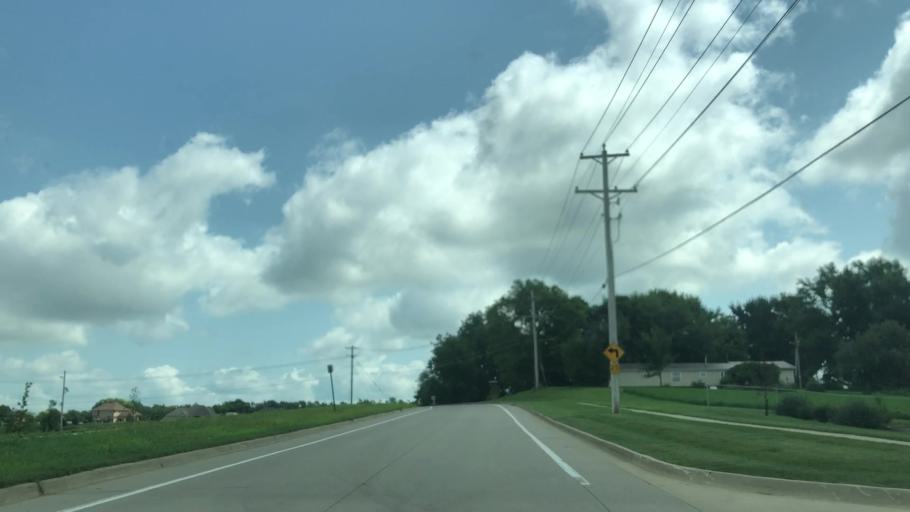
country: US
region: Iowa
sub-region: Marshall County
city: Marshalltown
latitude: 42.0179
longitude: -92.9475
